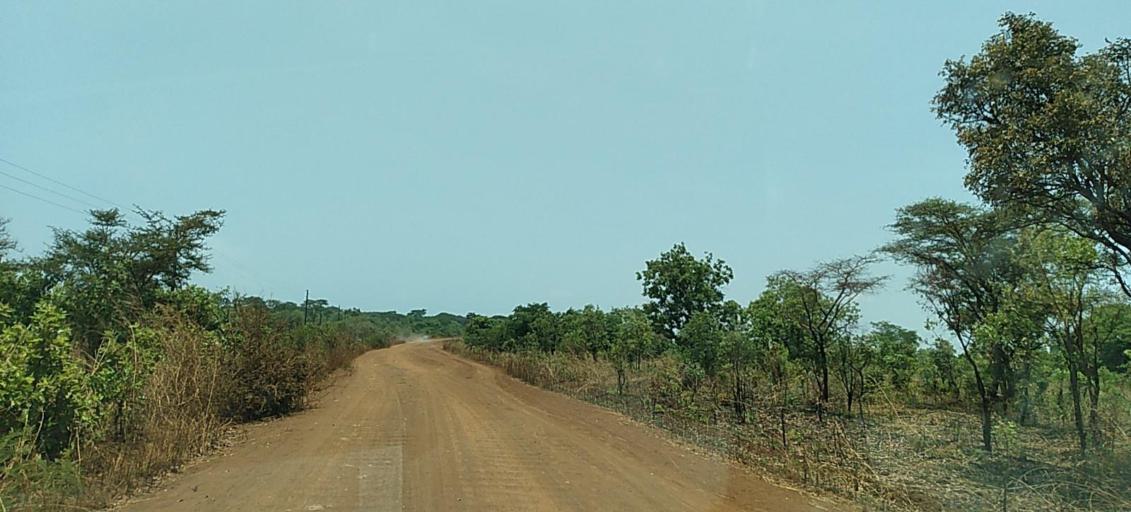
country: ZM
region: Copperbelt
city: Mpongwe
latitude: -13.6937
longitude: 27.8633
